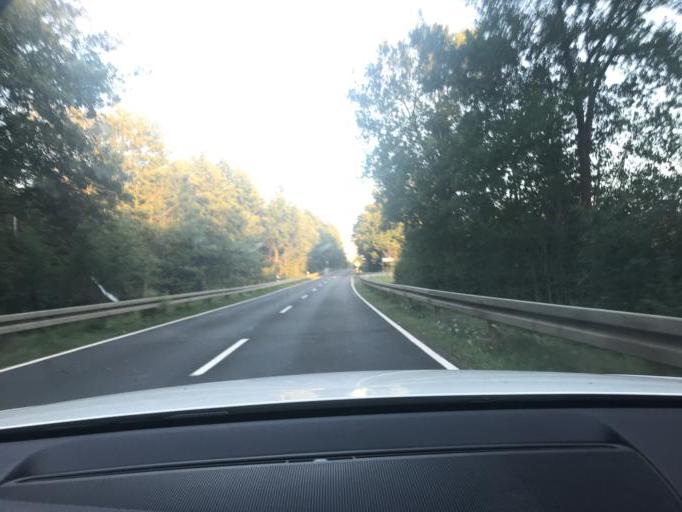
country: DE
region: Bavaria
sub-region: Upper Palatinate
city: Auerbach
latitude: 49.7014
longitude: 11.6273
